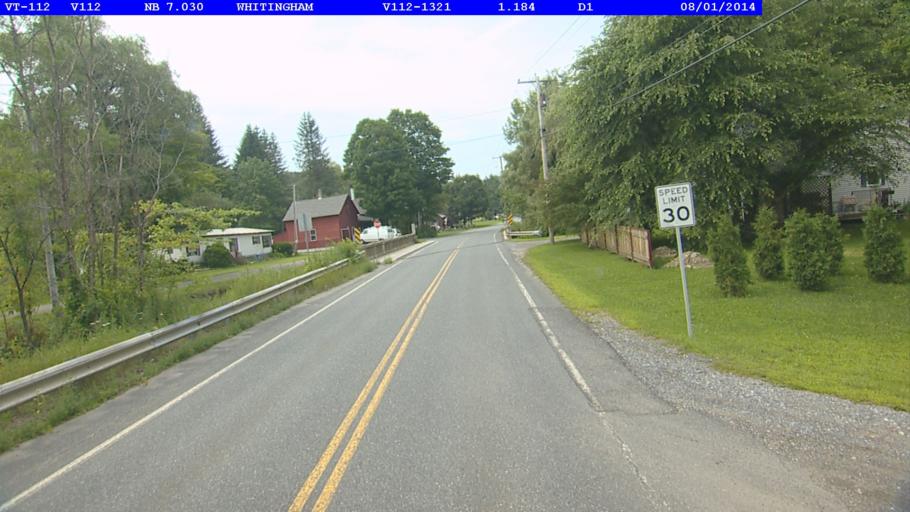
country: US
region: Vermont
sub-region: Windham County
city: Dover
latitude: 42.7911
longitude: -72.8200
